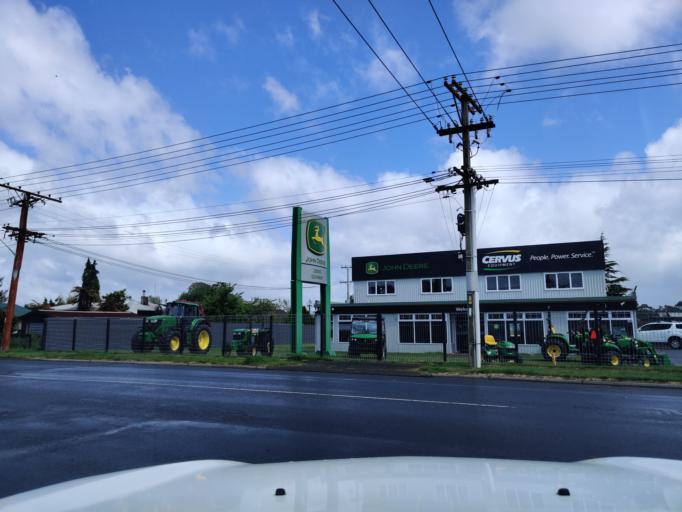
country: NZ
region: Bay of Plenty
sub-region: Rotorua District
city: Rotorua
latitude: -38.1449
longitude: 176.2764
